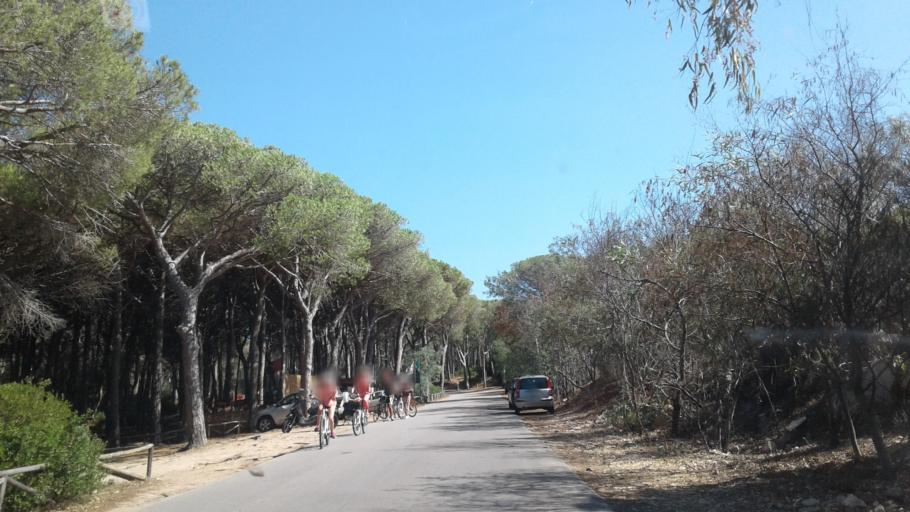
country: IT
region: Sardinia
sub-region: Provincia di Olbia-Tempio
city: La Maddalena
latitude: 41.2117
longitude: 9.4553
